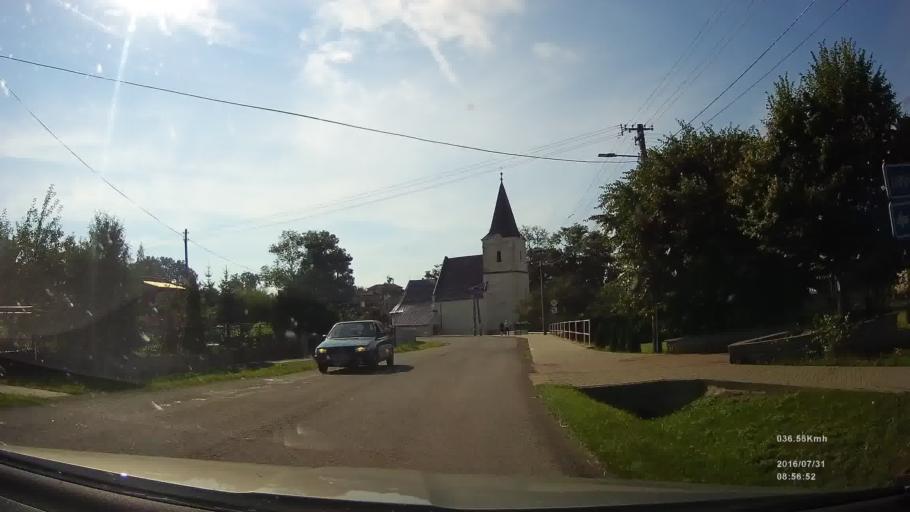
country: SK
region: Presovsky
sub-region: Okres Bardejov
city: Bardejov
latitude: 49.1501
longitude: 21.3225
